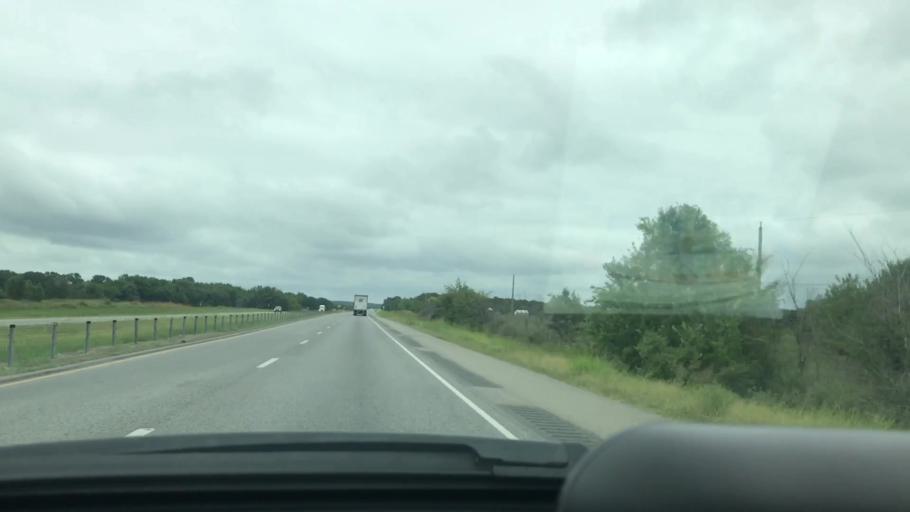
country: US
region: Oklahoma
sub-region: Pittsburg County
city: McAlester
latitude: 34.7582
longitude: -95.8913
